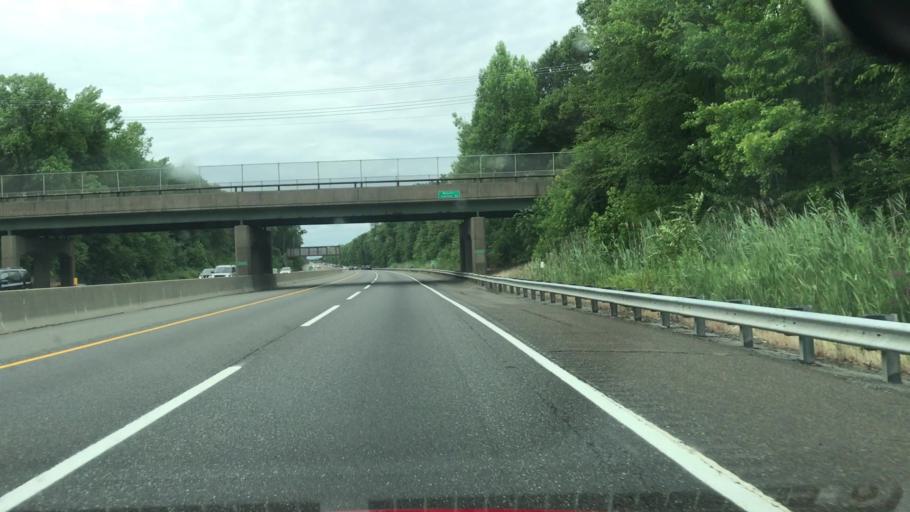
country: US
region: New Jersey
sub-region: Camden County
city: Bellmawr
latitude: 39.8502
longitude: -75.1086
